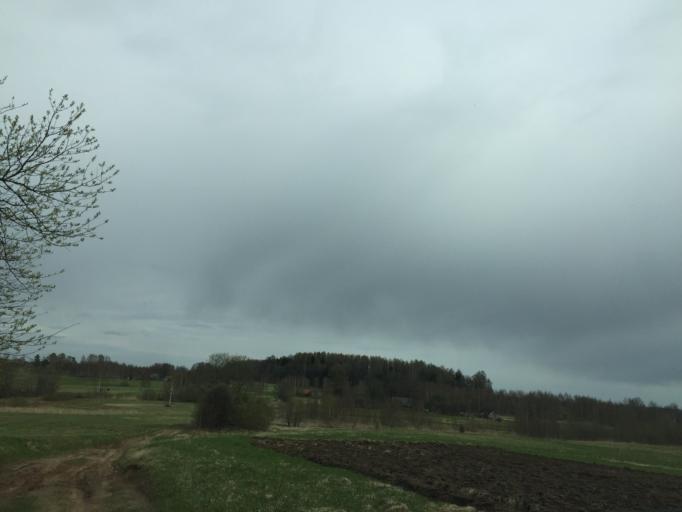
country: LV
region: Priekuli
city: Priekuli
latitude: 57.2932
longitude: 25.3316
